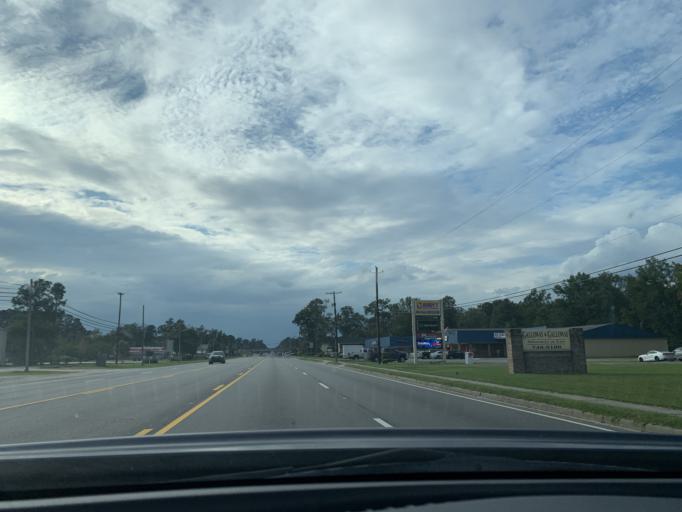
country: US
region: Georgia
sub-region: Chatham County
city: Pooler
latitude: 32.1202
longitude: -81.2606
